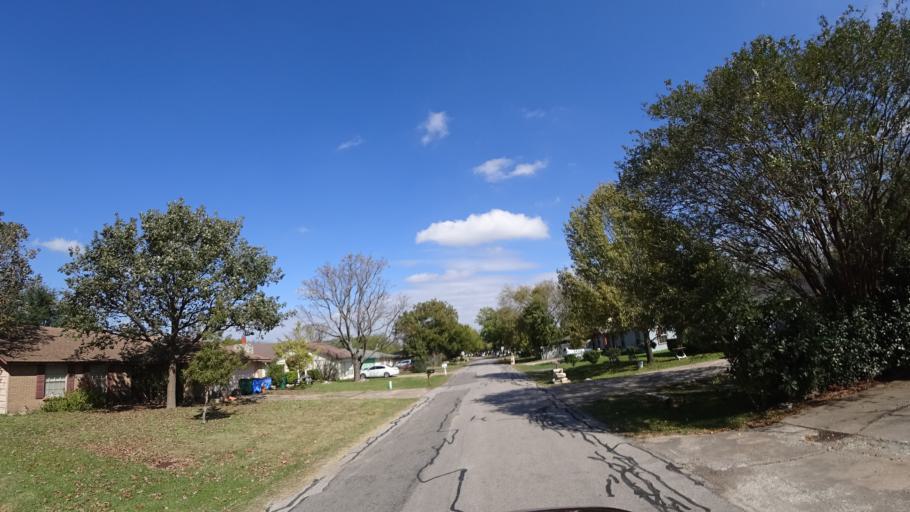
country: US
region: Texas
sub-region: Travis County
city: Windemere
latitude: 30.4492
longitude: -97.6447
